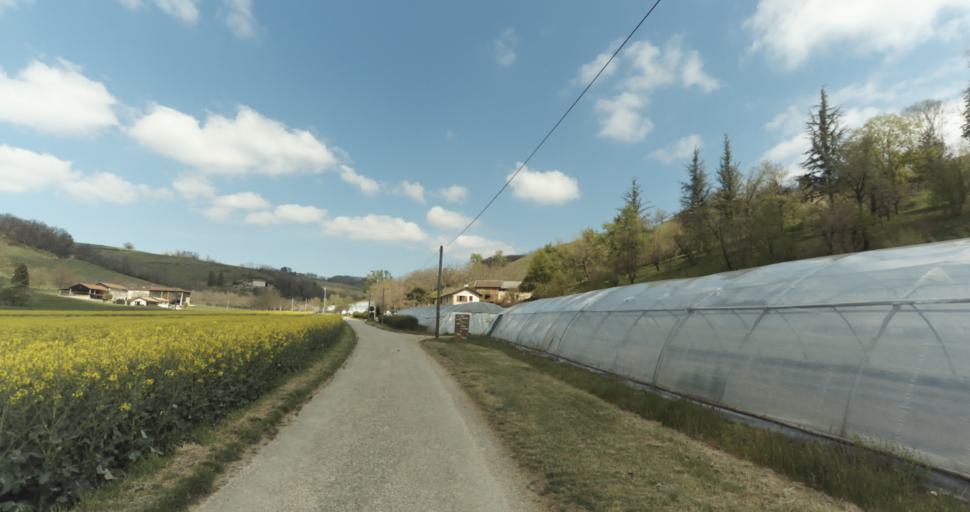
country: FR
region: Rhone-Alpes
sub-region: Departement de l'Isere
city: Saint-Verand
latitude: 45.1661
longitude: 5.3185
